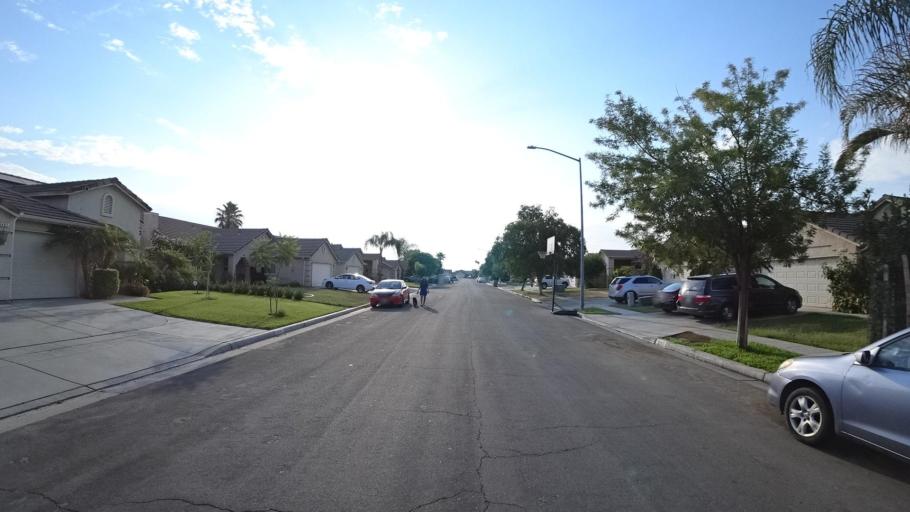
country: US
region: California
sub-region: Fresno County
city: Sunnyside
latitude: 36.7108
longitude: -119.7061
